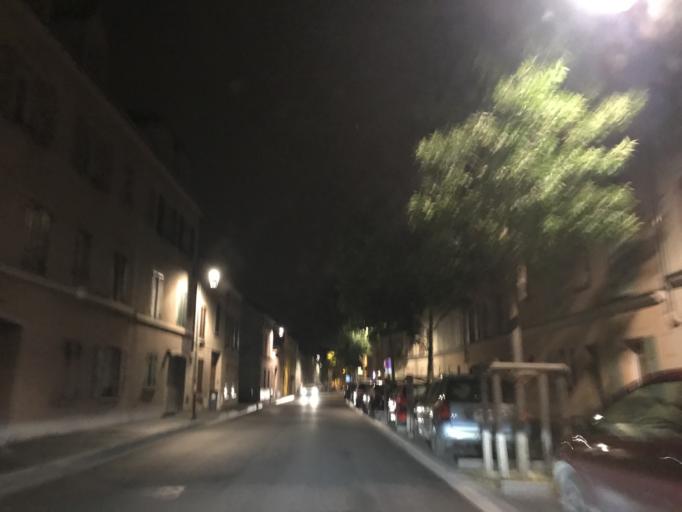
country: FR
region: Ile-de-France
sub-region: Departement des Yvelines
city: Maisons-Laffitte
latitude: 48.9434
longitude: 2.1647
